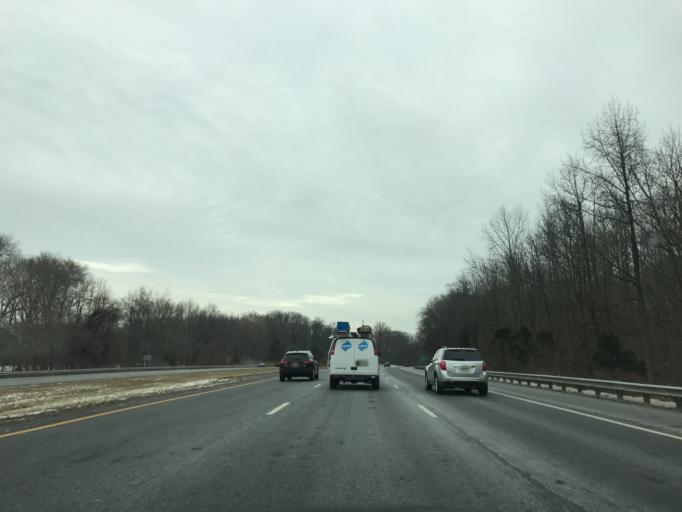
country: US
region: New Jersey
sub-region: Burlington County
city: Burlington
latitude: 40.0601
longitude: -74.8128
